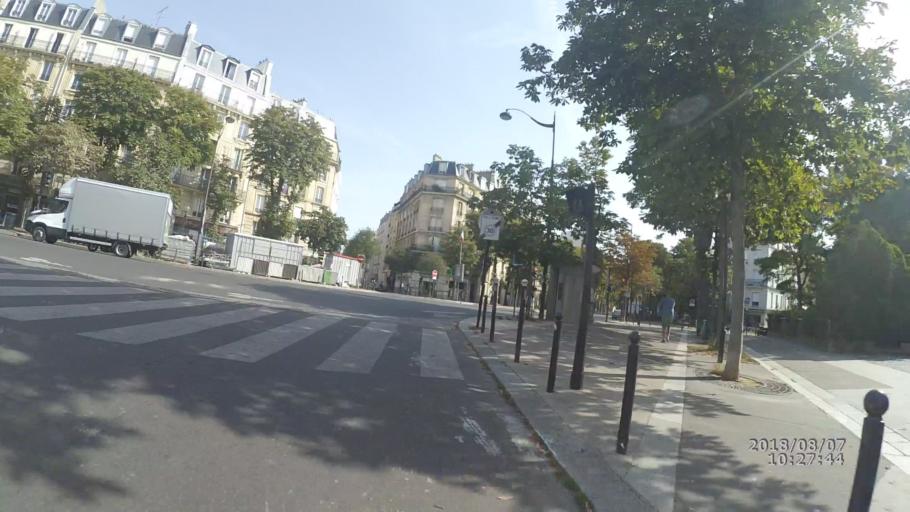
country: FR
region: Ile-de-France
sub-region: Paris
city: Paris
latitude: 48.8350
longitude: 2.3464
